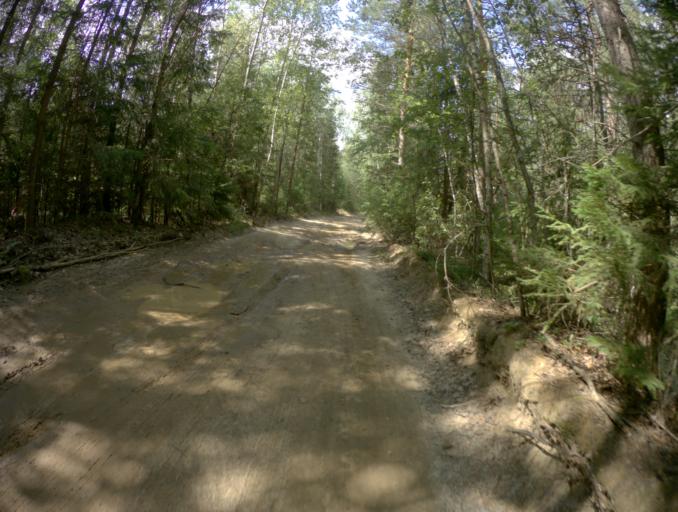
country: RU
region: Vladimir
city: Raduzhnyy
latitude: 55.9670
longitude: 40.2347
